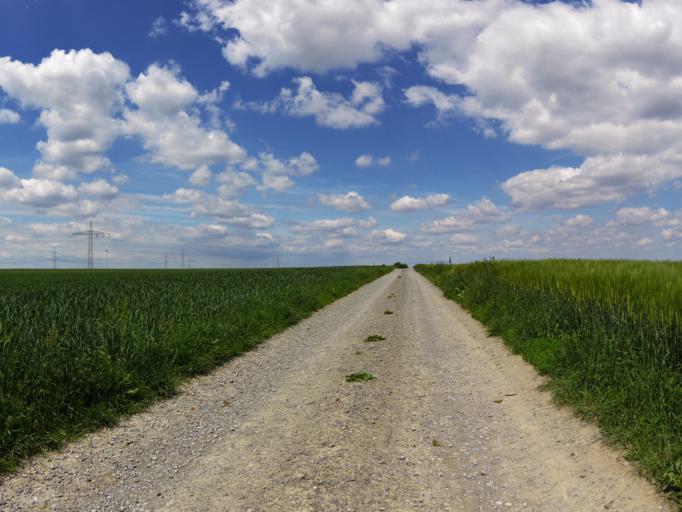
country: DE
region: Bavaria
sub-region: Regierungsbezirk Unterfranken
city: Theilheim
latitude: 49.7360
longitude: 10.0647
